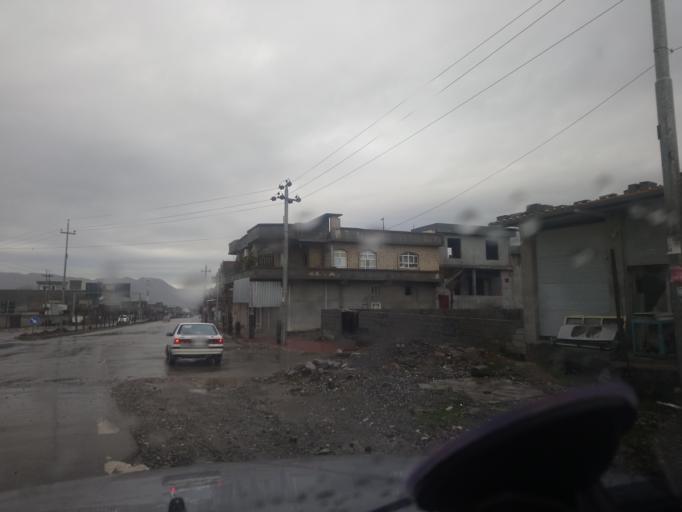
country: IQ
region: As Sulaymaniyah
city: Qeladize
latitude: 36.1779
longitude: 45.1550
